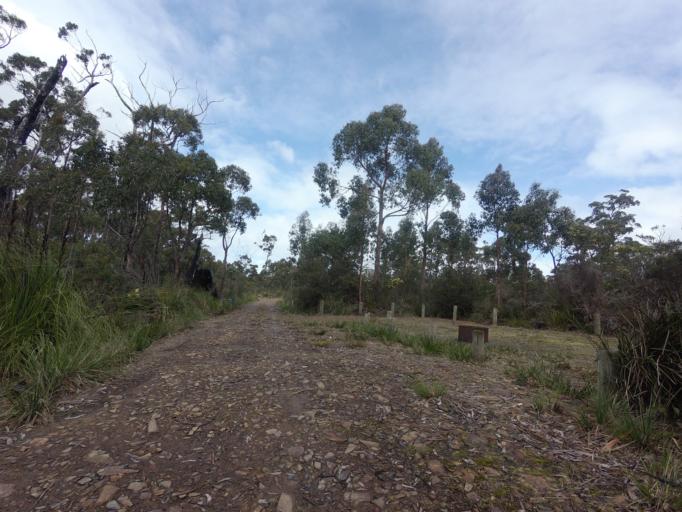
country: AU
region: Tasmania
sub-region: Huon Valley
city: Geeveston
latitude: -43.4801
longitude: 146.9391
